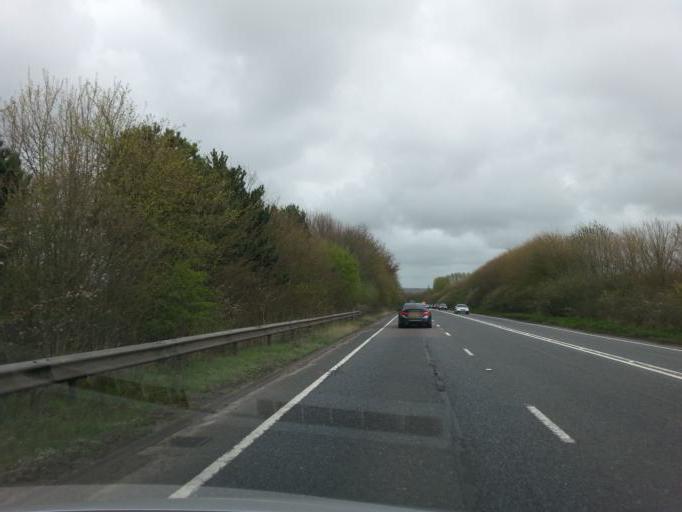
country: GB
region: England
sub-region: Somerset
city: South Petherton
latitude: 50.9392
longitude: -2.8222
